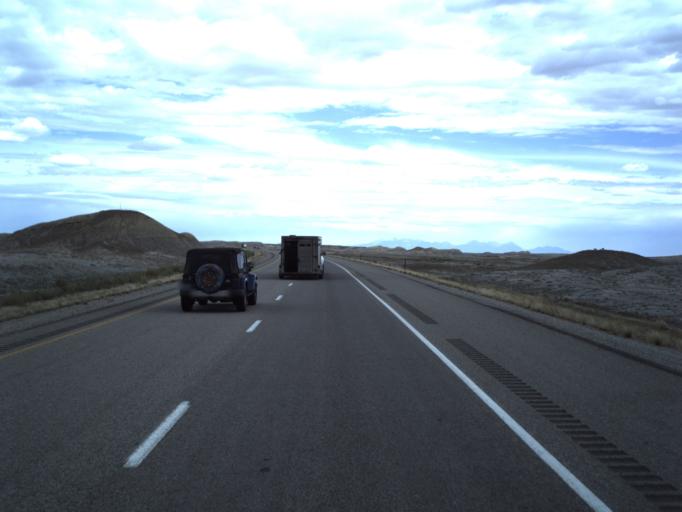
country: US
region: Utah
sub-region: Grand County
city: Moab
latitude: 38.9346
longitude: -110.0241
